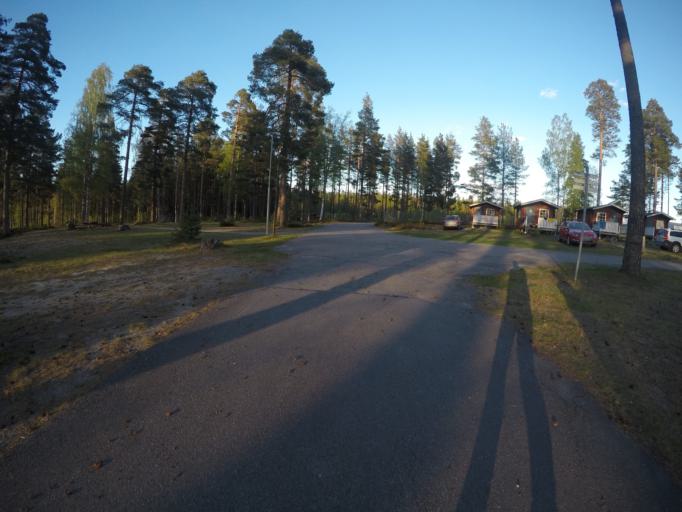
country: SE
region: Gaevleborg
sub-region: Hudiksvalls Kommun
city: Iggesund
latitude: 61.6591
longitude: 17.0794
